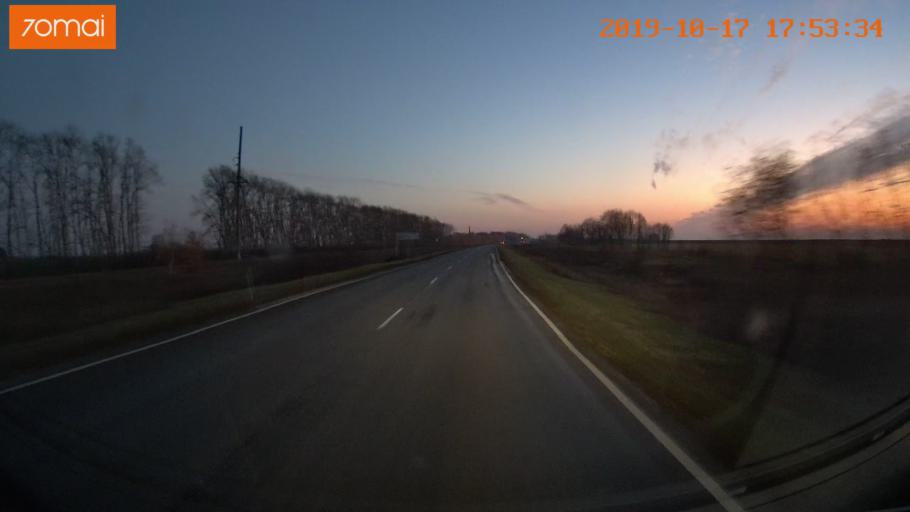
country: RU
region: Tula
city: Kurkino
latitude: 53.6133
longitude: 38.6736
